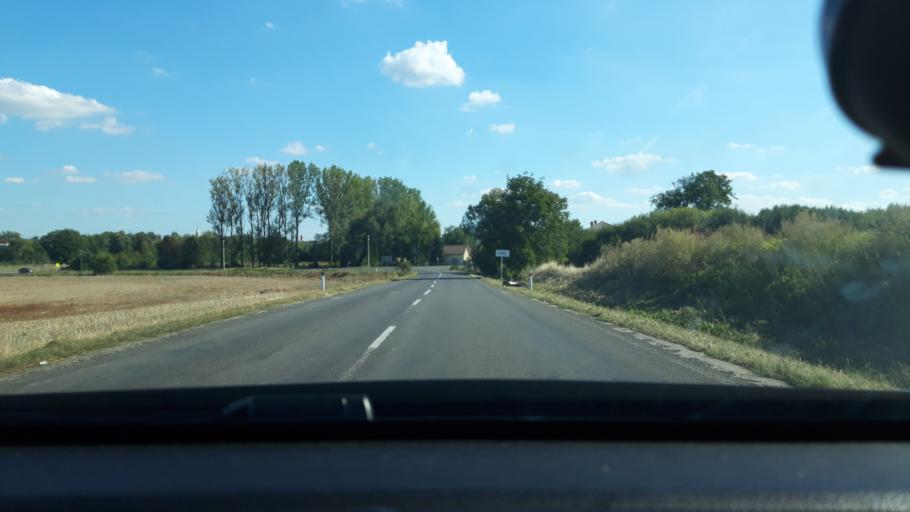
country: SK
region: Kosicky
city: Secovce
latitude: 48.6082
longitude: 21.6182
